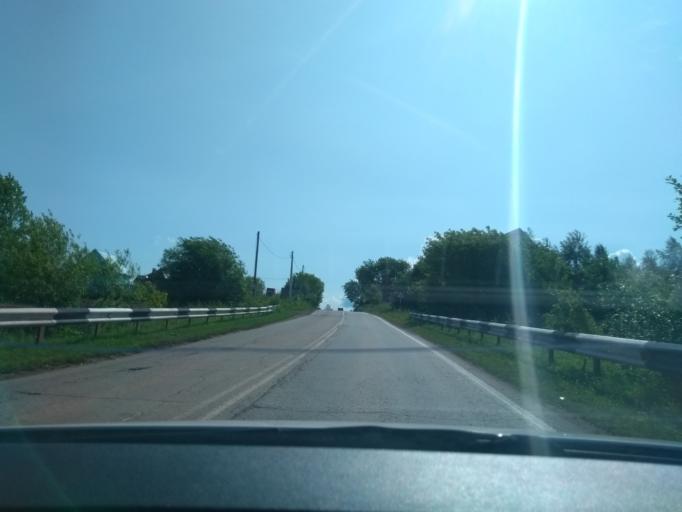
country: RU
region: Perm
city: Lobanovo
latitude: 57.8494
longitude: 56.3415
